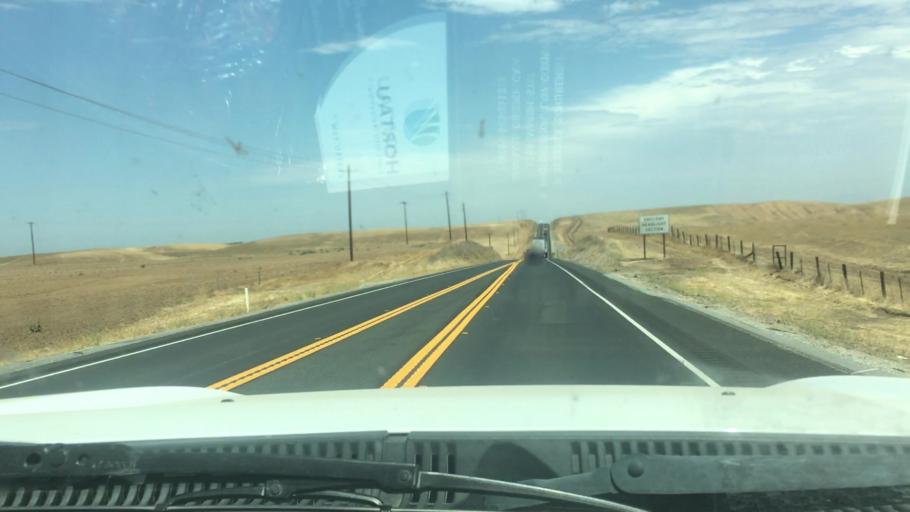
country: US
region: California
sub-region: Tulare County
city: Richgrove
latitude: 35.7641
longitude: -119.0532
